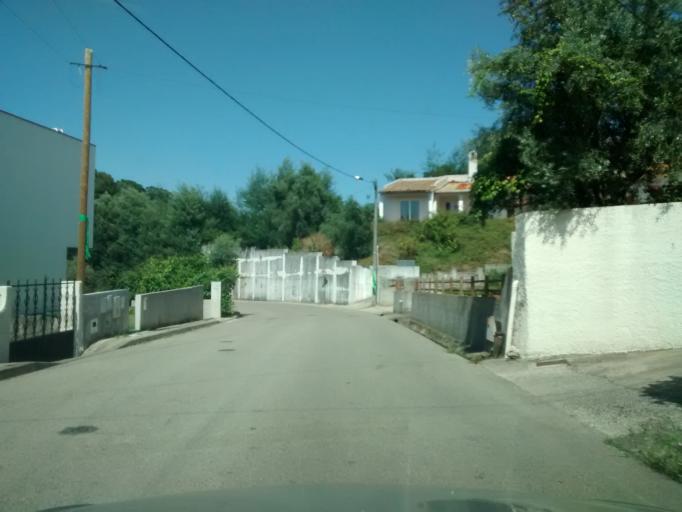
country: PT
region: Aveiro
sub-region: Mealhada
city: Mealhada
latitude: 40.3860
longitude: -8.3862
